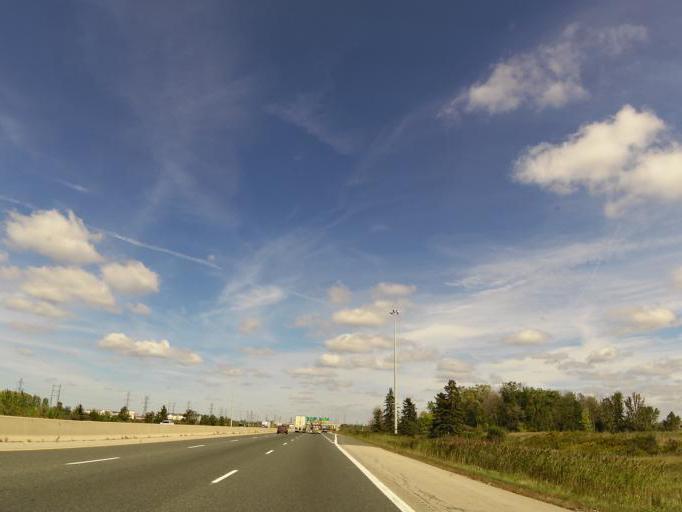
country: CA
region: Ontario
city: London
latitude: 42.9168
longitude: -81.2190
